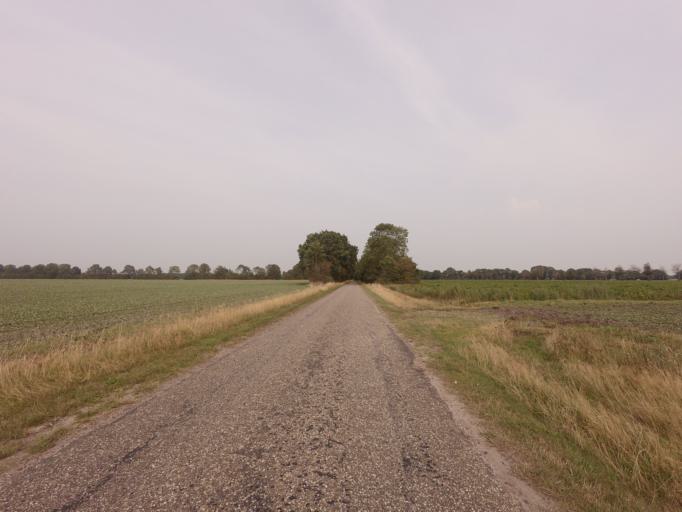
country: NL
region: Drenthe
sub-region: Gemeente Tynaarlo
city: Vries
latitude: 53.1031
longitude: 6.5466
